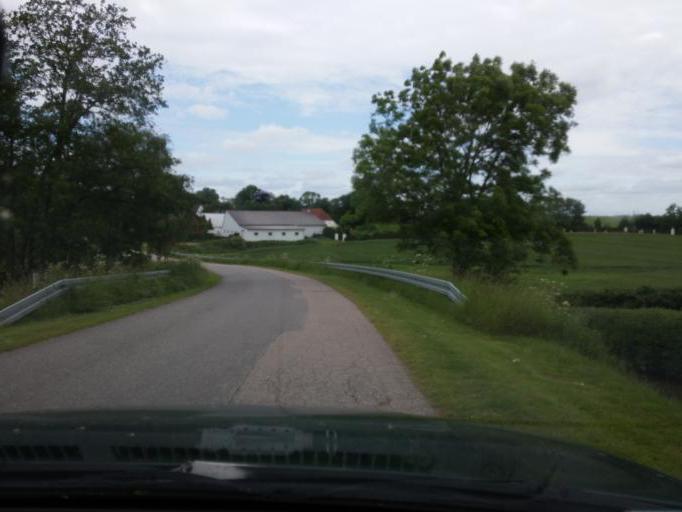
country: DK
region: South Denmark
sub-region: Aabenraa Kommune
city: Lojt Kirkeby
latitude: 55.1364
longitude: 9.4930
